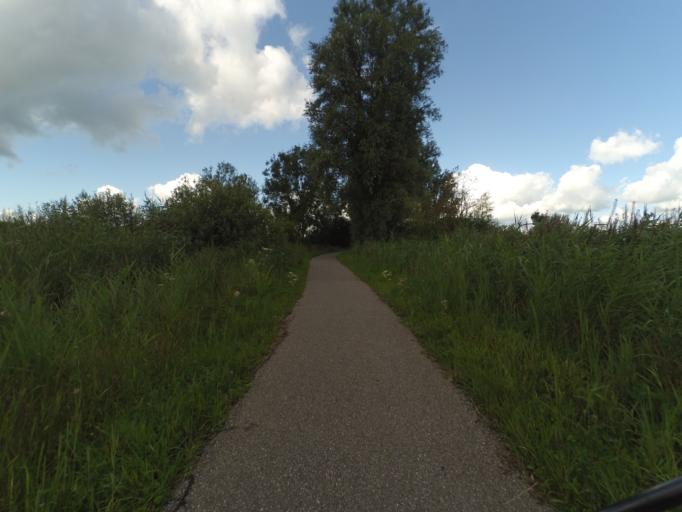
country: NL
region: Friesland
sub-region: Gemeente Dantumadiel
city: De Westereen
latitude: 53.2628
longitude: 6.0216
